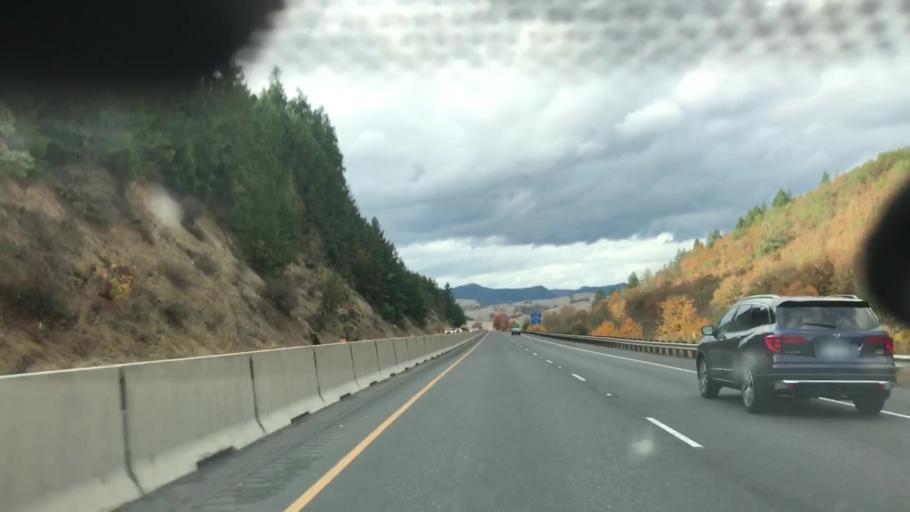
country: US
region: Oregon
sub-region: Douglas County
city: Sutherlin
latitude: 43.4413
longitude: -123.3174
